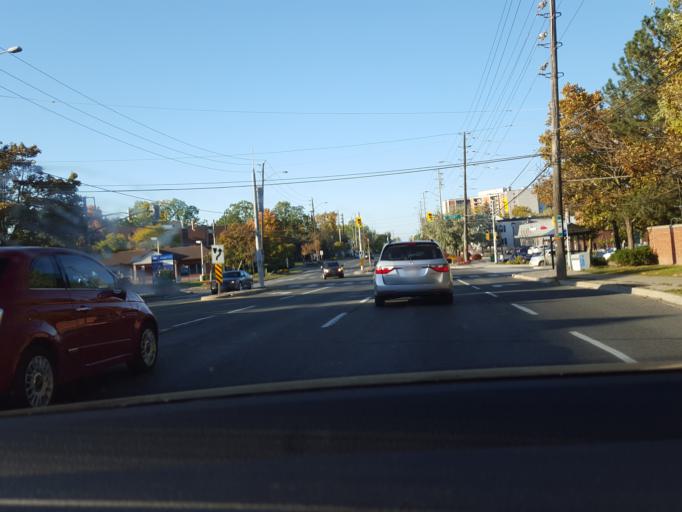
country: CA
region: Ontario
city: North York
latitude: 43.8137
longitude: -79.4238
